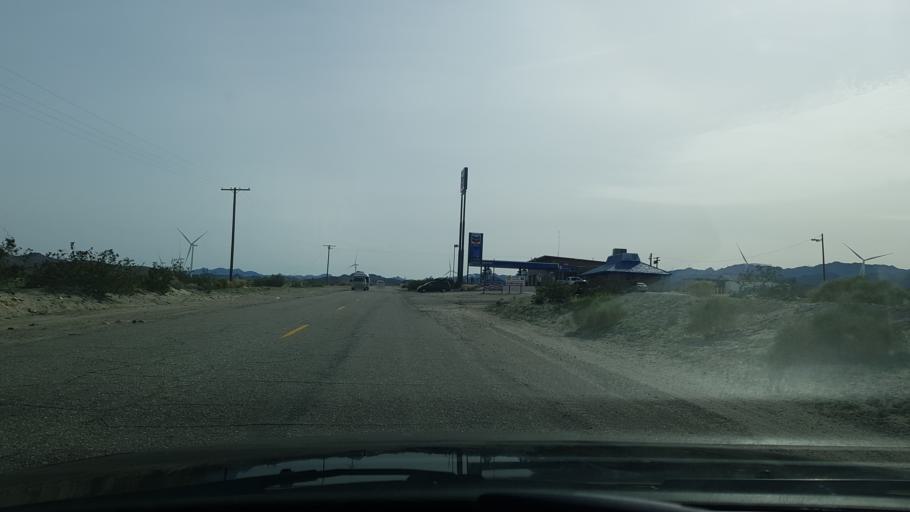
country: US
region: California
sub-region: Imperial County
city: Seeley
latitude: 32.7321
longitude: -115.9943
